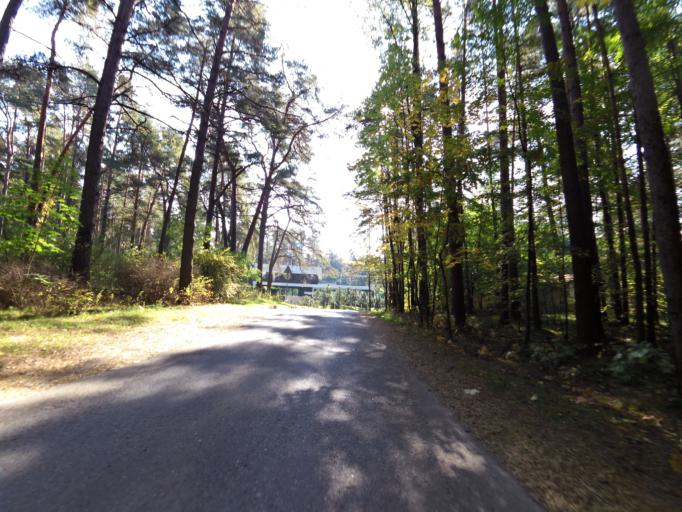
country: LT
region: Vilnius County
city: Rasos
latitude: 54.7311
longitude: 25.3126
